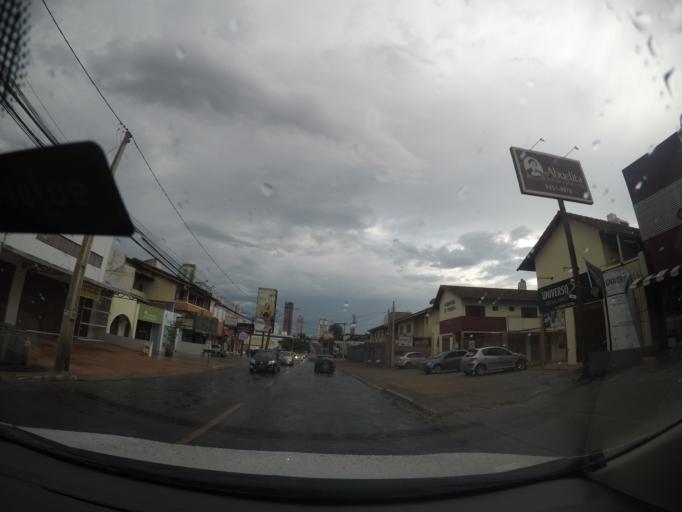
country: BR
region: Goias
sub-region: Goiania
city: Goiania
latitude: -16.7100
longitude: -49.2745
